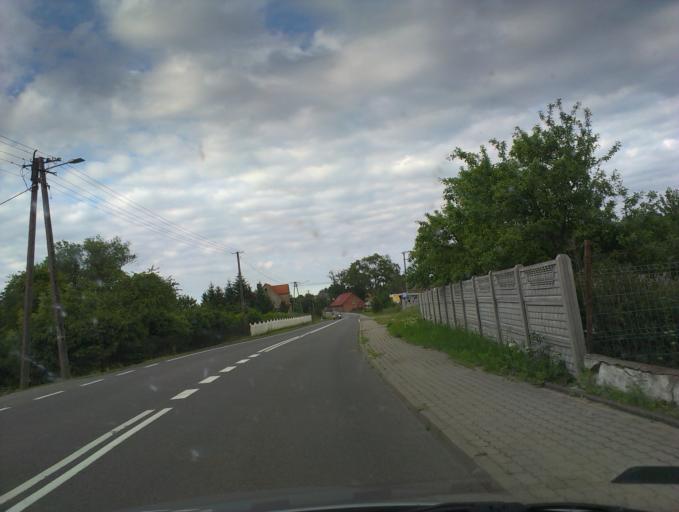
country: PL
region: West Pomeranian Voivodeship
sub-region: Powiat szczecinecki
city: Szczecinek
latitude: 53.6601
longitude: 16.6689
